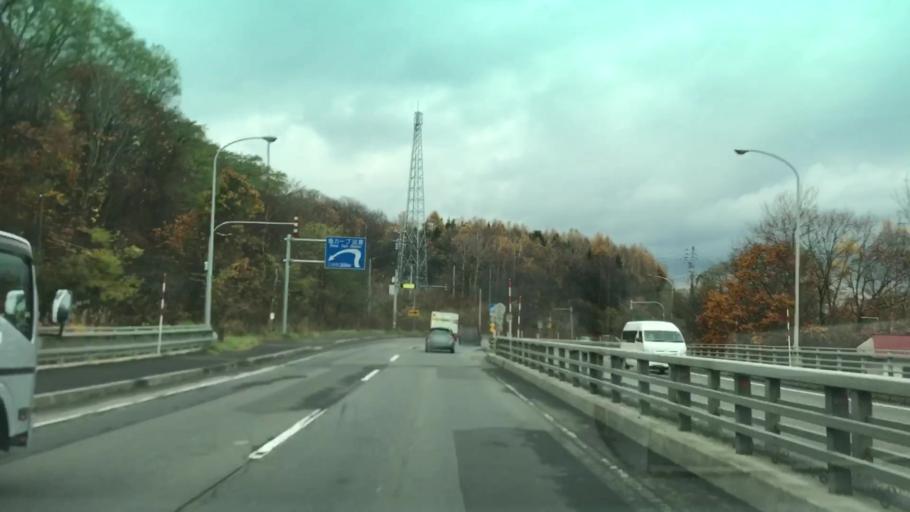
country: JP
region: Hokkaido
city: Otaru
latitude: 43.1694
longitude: 141.0850
